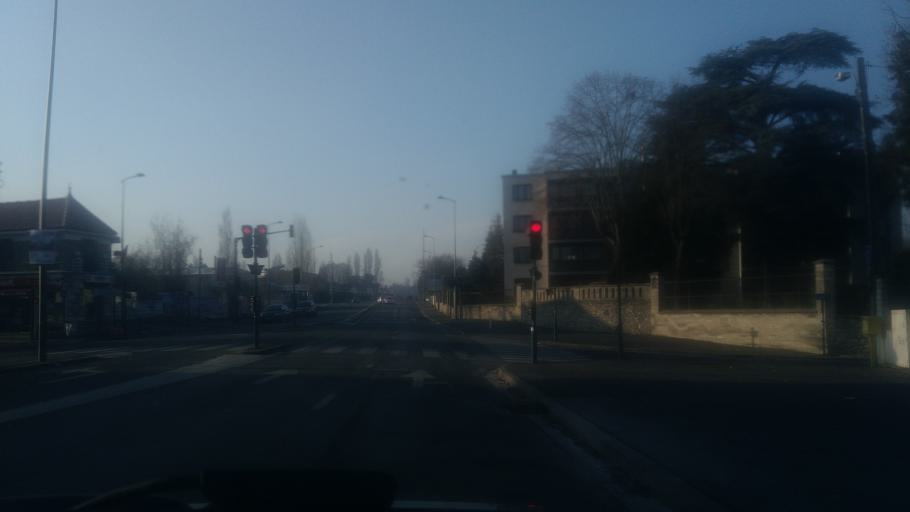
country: FR
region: Ile-de-France
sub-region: Departement du Val-d'Oise
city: Pontoise
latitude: 49.0449
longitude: 2.0889
